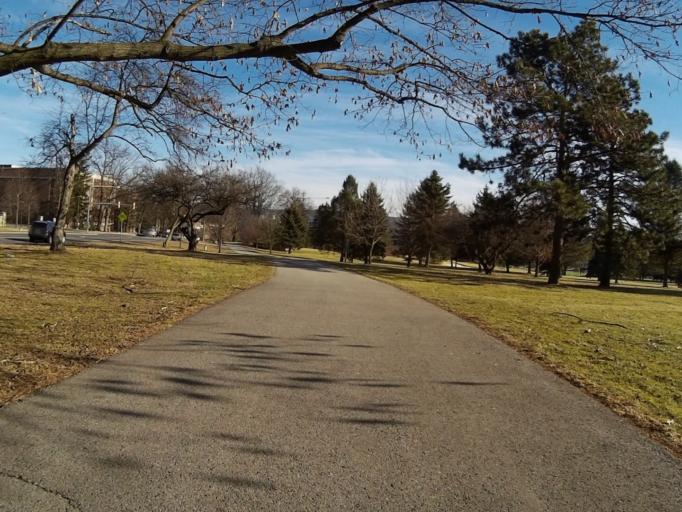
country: US
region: Pennsylvania
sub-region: Centre County
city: State College
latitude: 40.7961
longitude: -77.8717
